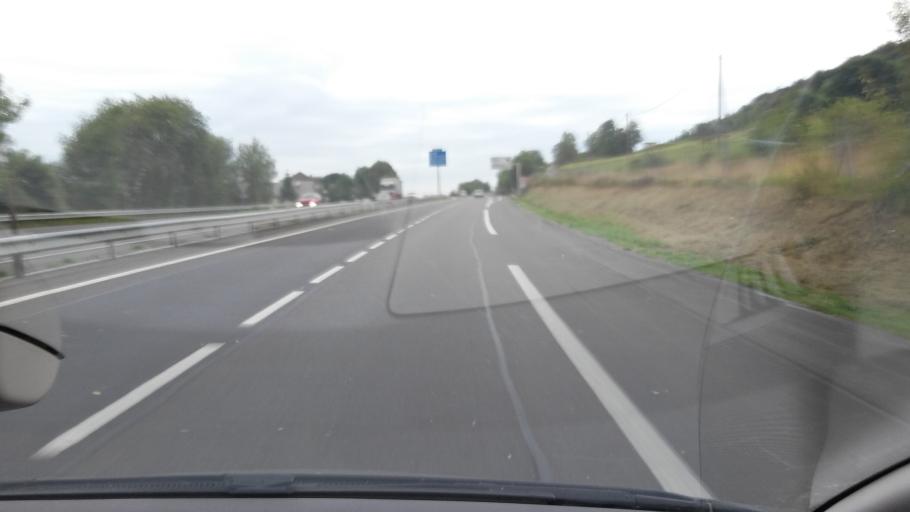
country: FR
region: Champagne-Ardenne
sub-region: Departement des Ardennes
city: La Francheville
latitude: 49.6748
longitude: 4.6558
